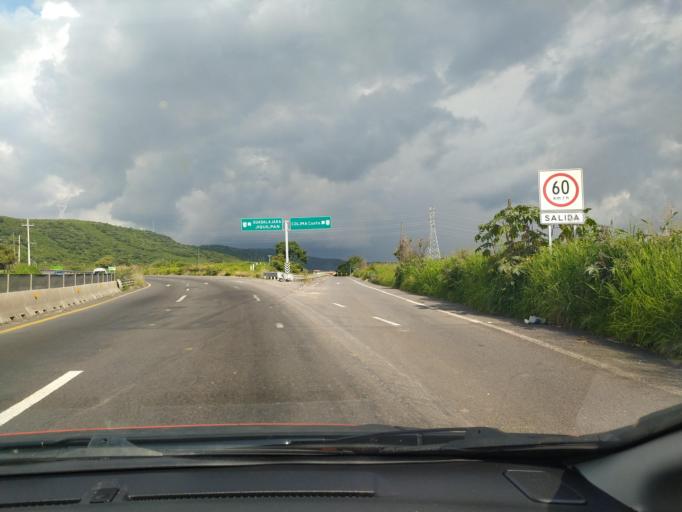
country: MX
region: Jalisco
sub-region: Acatlan de Juarez
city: Villa de los Ninos
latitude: 20.4240
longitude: -103.5584
